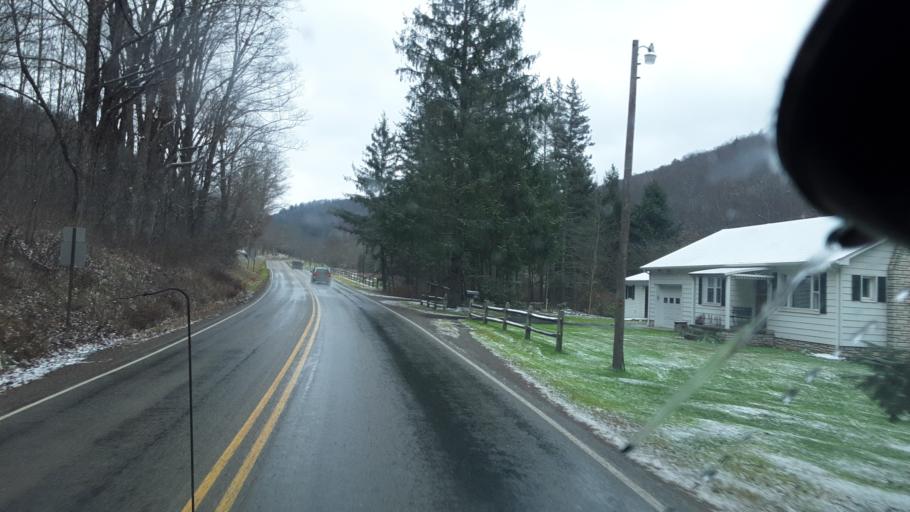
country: US
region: Pennsylvania
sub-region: Potter County
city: Coudersport
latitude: 41.8159
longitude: -78.0093
